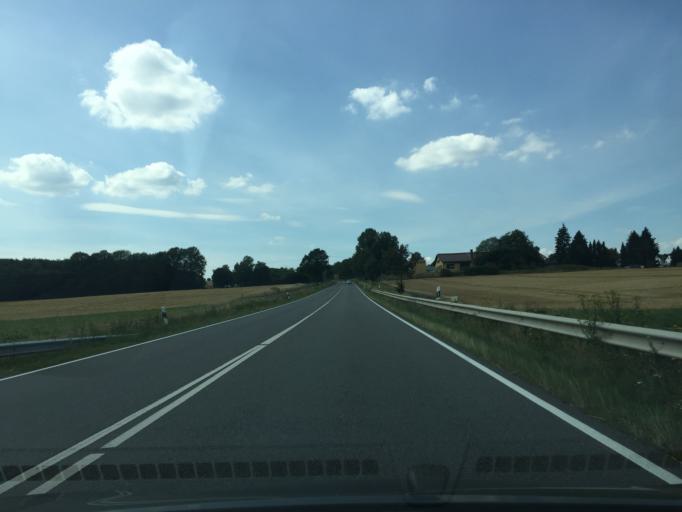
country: DE
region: Rheinland-Pfalz
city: Nomborn
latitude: 50.4411
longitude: 7.9101
